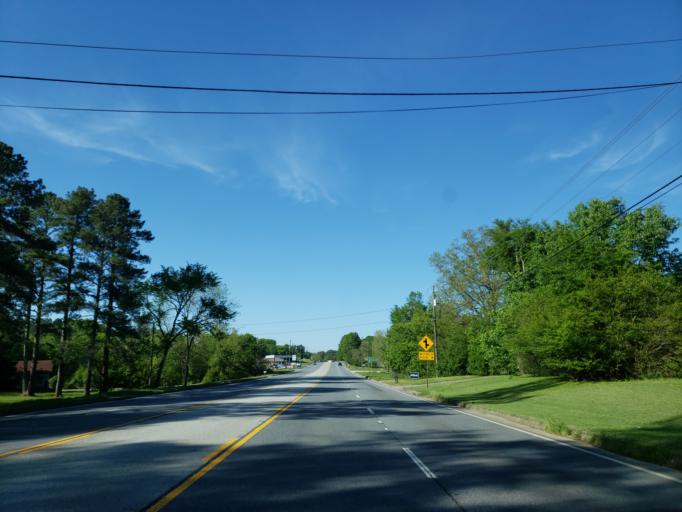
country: US
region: Georgia
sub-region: Polk County
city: Cedartown
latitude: 33.9693
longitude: -85.2600
